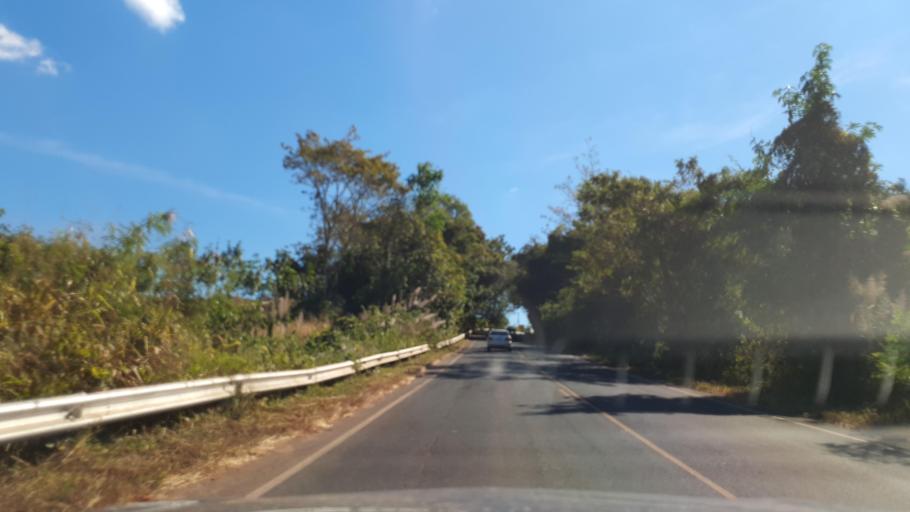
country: TH
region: Kalasin
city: Khao Wong
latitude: 16.7719
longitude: 104.1539
